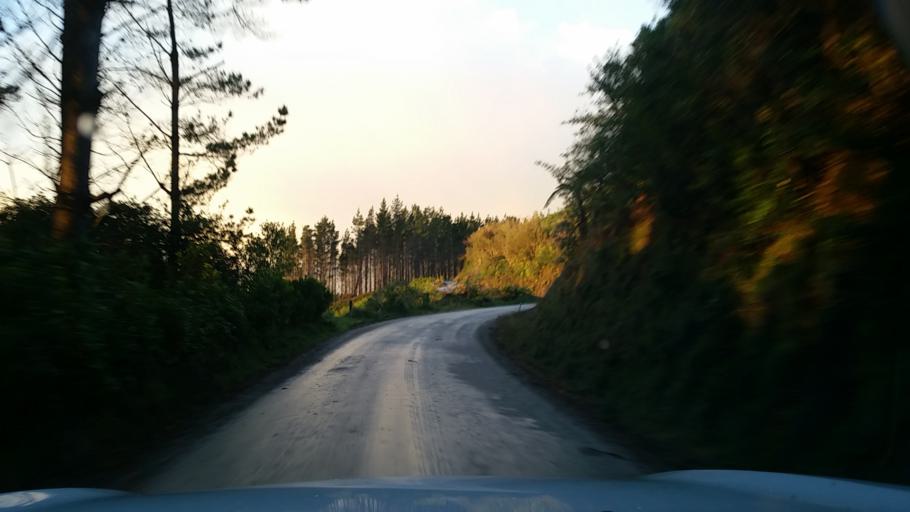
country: NZ
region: Manawatu-Wanganui
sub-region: Wanganui District
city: Wanganui
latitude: -39.7745
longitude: 174.8599
